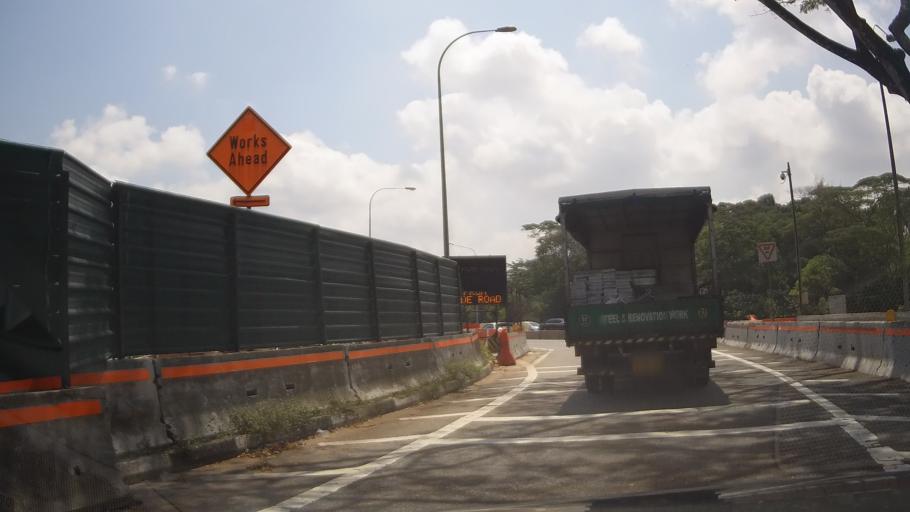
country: SG
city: Singapore
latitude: 1.3338
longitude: 103.8169
